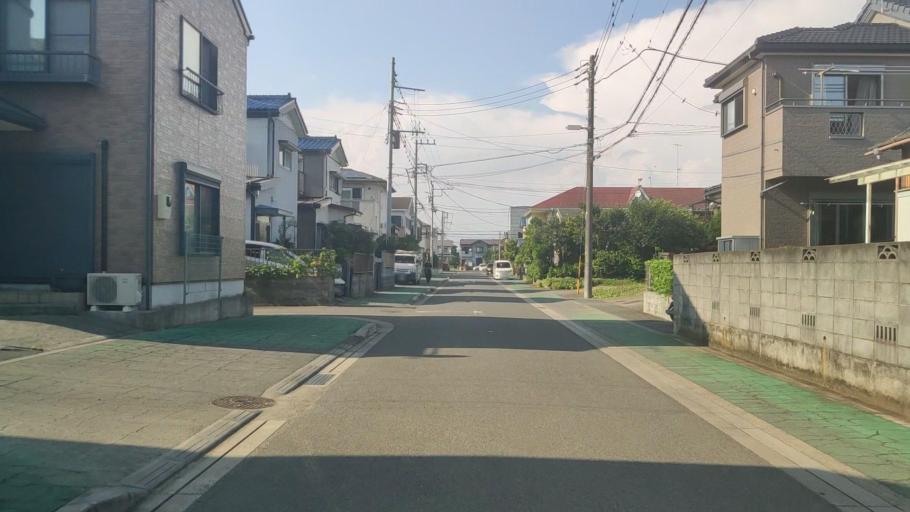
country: JP
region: Kanagawa
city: Hiratsuka
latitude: 35.3484
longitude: 139.3225
